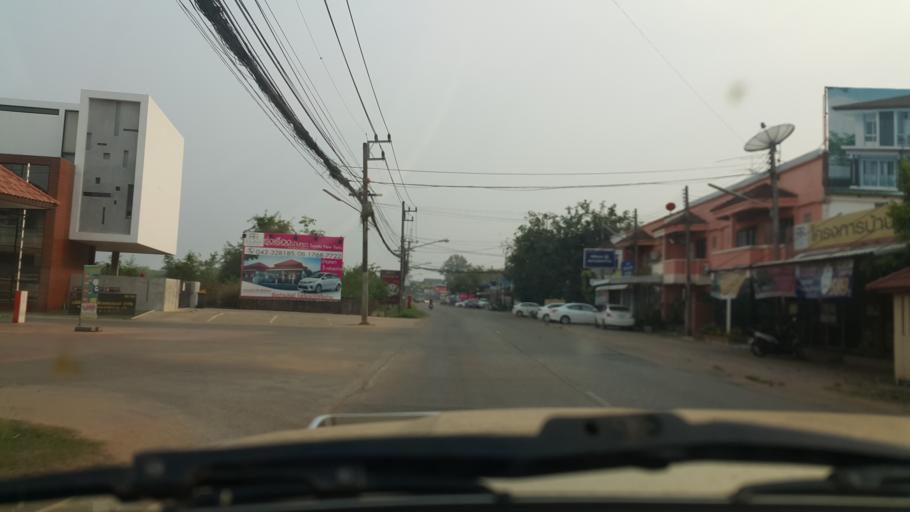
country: TH
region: Changwat Udon Thani
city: Udon Thani
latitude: 17.3976
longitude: 102.7714
